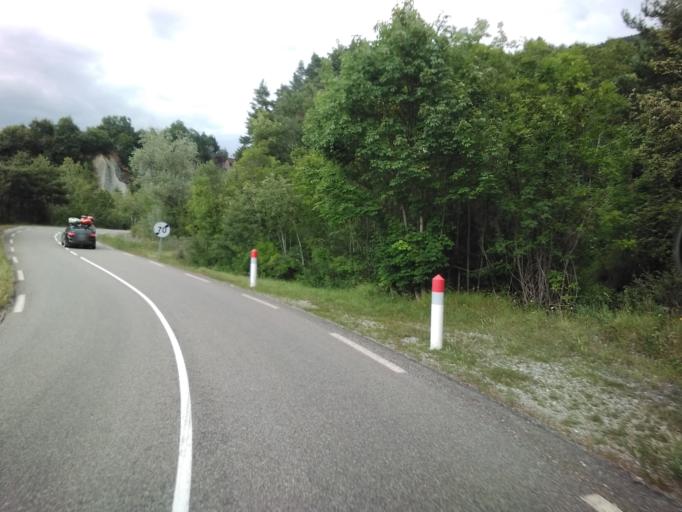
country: FR
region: Provence-Alpes-Cote d'Azur
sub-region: Departement des Hautes-Alpes
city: Chorges
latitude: 44.4960
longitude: 6.3436
